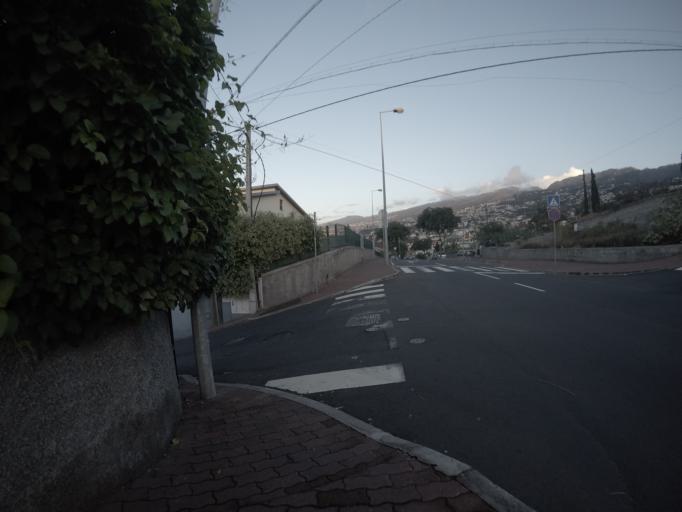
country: PT
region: Madeira
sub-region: Funchal
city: Funchal
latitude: 32.6488
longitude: -16.8957
